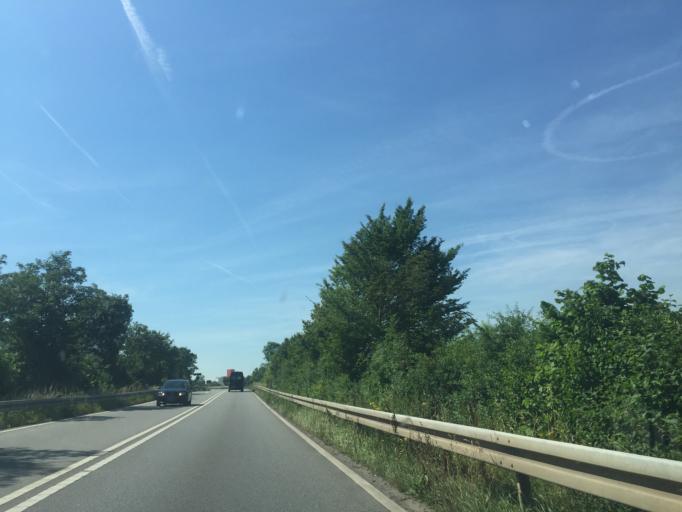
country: DE
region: Baden-Wuerttemberg
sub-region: Karlsruhe Region
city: Eppelheim
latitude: 49.4151
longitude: 8.6464
